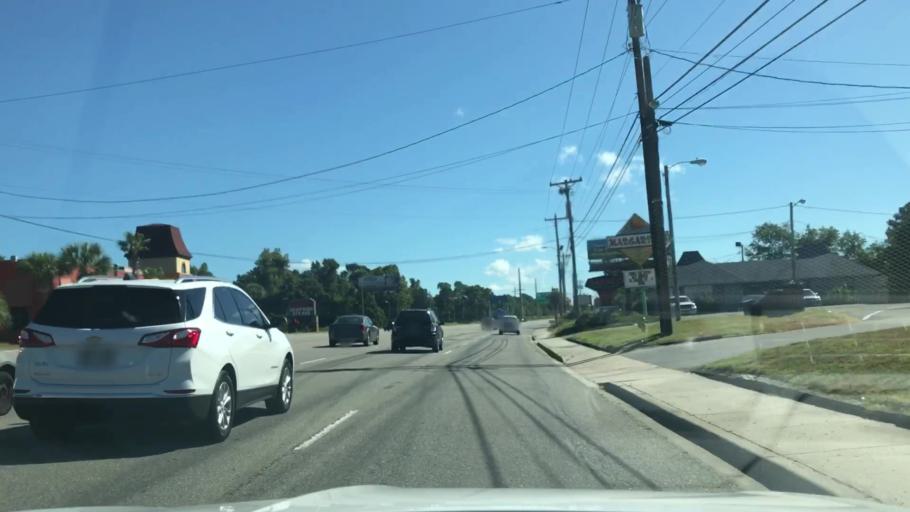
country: US
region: South Carolina
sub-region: Horry County
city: North Myrtle Beach
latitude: 33.7835
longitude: -78.7855
